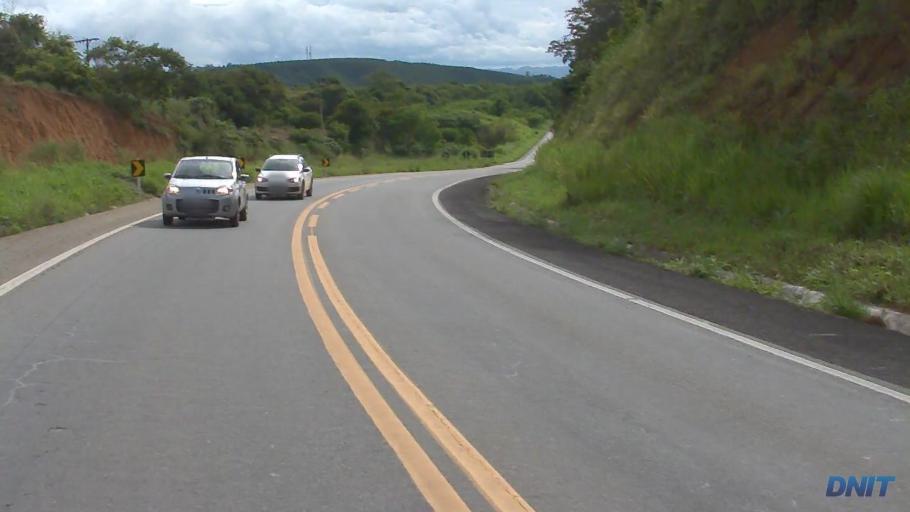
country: BR
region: Minas Gerais
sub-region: Ipaba
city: Ipaba
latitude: -19.2951
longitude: -42.3591
